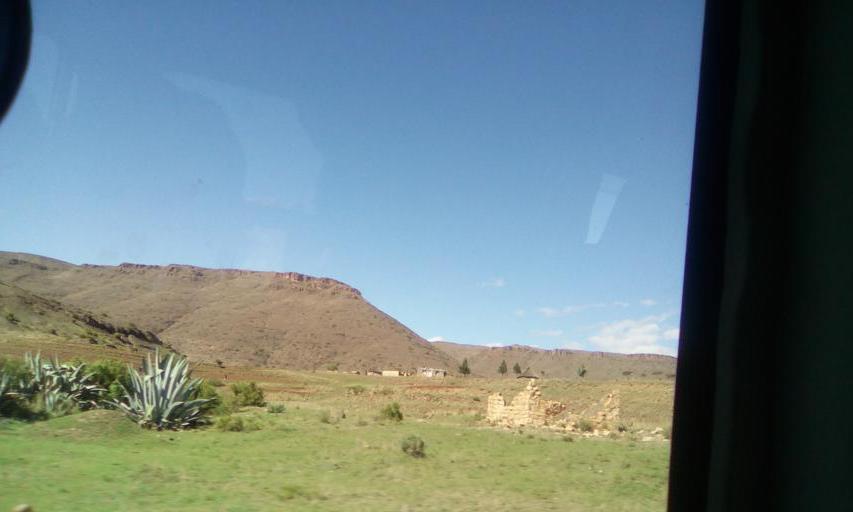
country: LS
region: Qacha's Nek
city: Qacha's Nek
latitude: -30.0561
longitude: 28.2974
